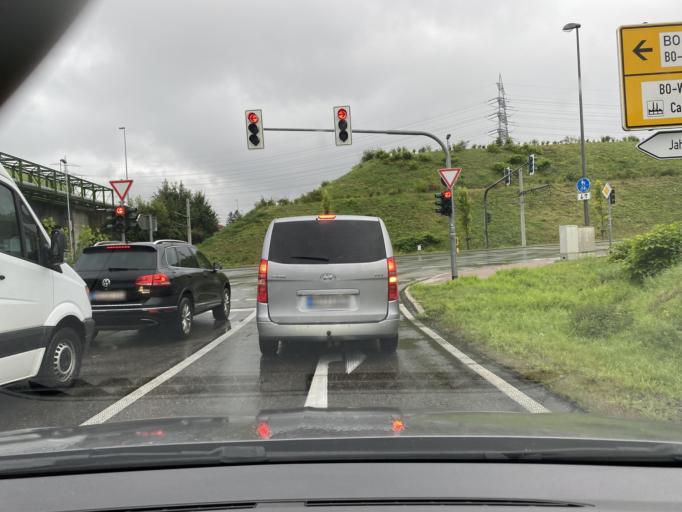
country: DE
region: North Rhine-Westphalia
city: Bochum-Hordel
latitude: 51.4819
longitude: 7.1810
